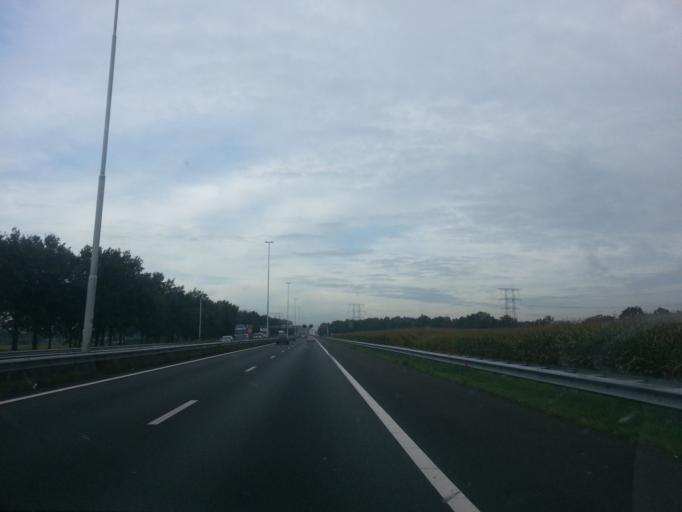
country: NL
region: North Brabant
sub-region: Gemeente Oisterwijk
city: Oisterwijk
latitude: 51.5261
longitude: 5.2133
